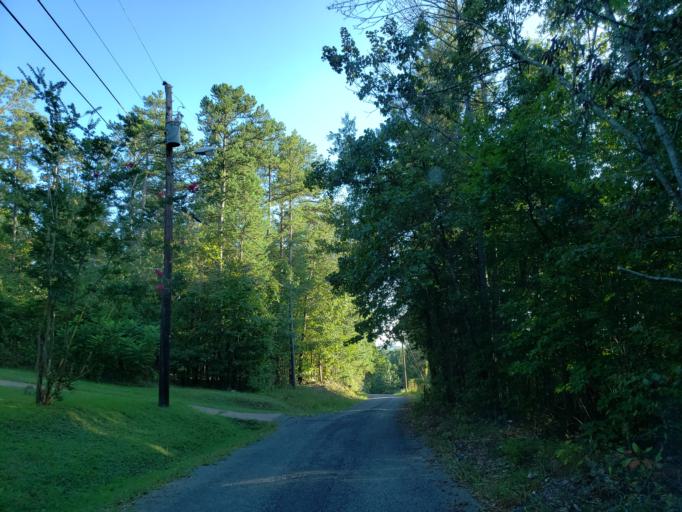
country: US
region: Georgia
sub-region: Bartow County
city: Euharlee
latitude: 34.2437
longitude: -84.9441
